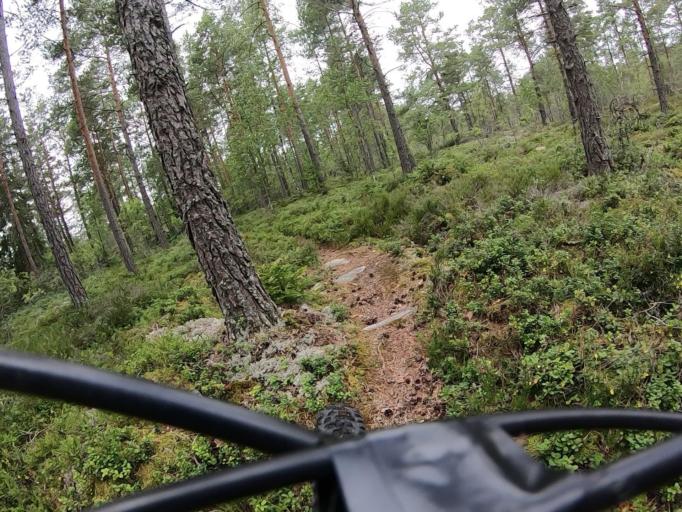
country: FI
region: Varsinais-Suomi
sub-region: Vakka-Suomi
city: Uusikaupunki
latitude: 60.8378
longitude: 21.3952
